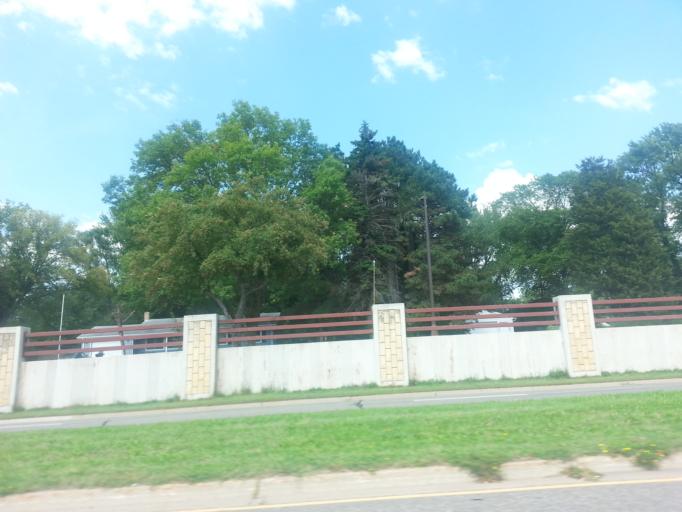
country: US
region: Minnesota
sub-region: Ramsey County
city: Maplewood
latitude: 44.9557
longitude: -92.9880
